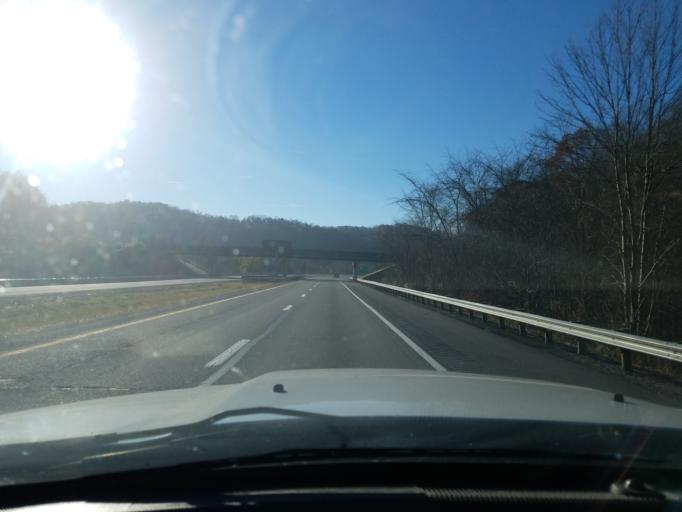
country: US
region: West Virginia
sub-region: Jackson County
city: Ravenswood
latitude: 38.9484
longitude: -81.7040
